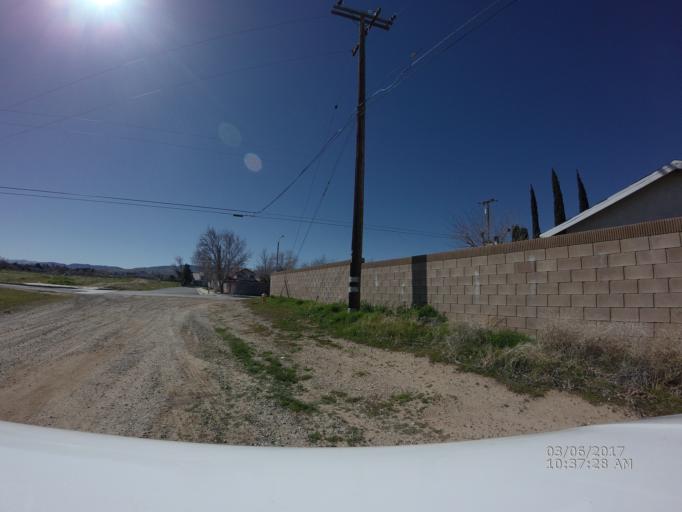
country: US
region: California
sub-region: Los Angeles County
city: Quartz Hill
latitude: 34.6568
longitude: -118.2210
